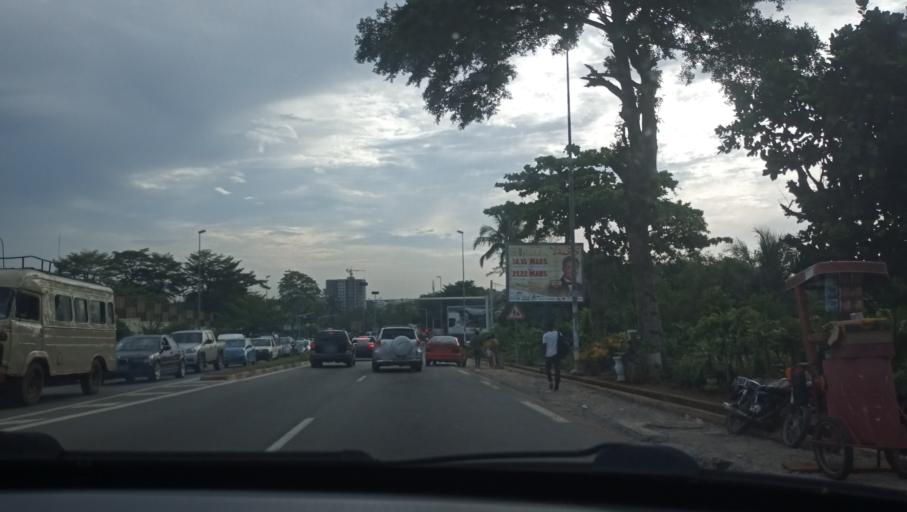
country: CI
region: Lagunes
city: Abidjan
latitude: 5.3488
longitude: -4.0012
